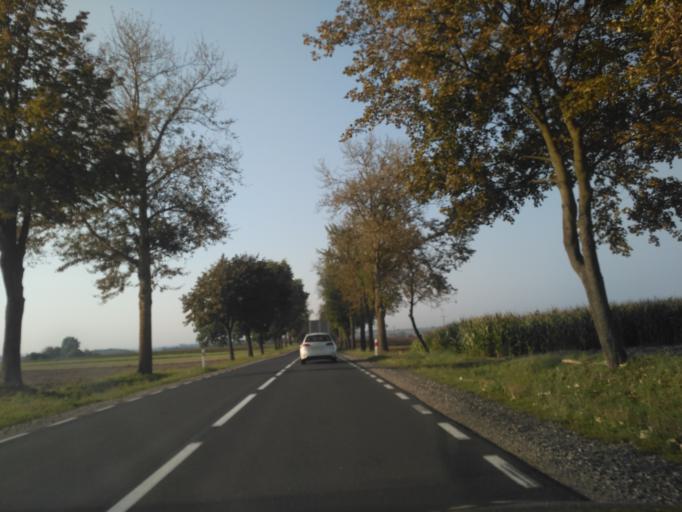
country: PL
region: Lublin Voivodeship
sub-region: Powiat krasnicki
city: Szastarka
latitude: 50.8121
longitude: 22.3194
